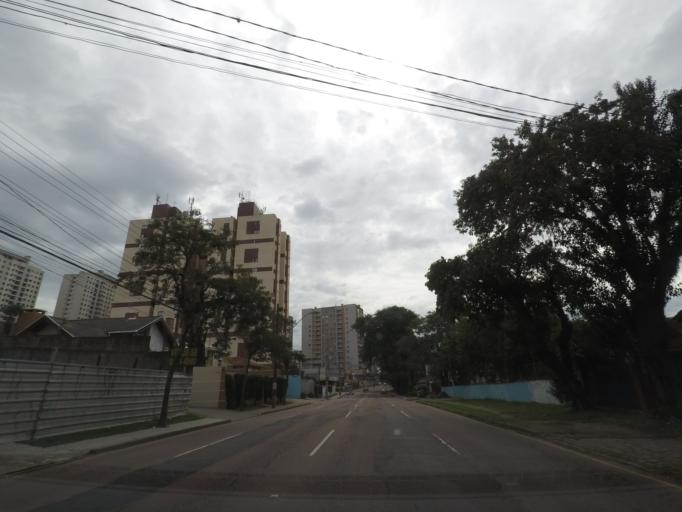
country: BR
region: Parana
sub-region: Curitiba
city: Curitiba
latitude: -25.5006
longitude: -49.2947
